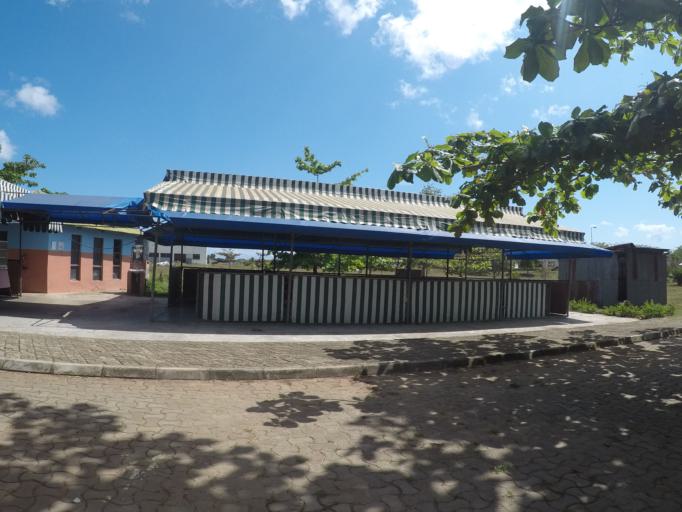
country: TZ
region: Zanzibar Central/South
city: Koani
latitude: -6.2001
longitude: 39.3077
